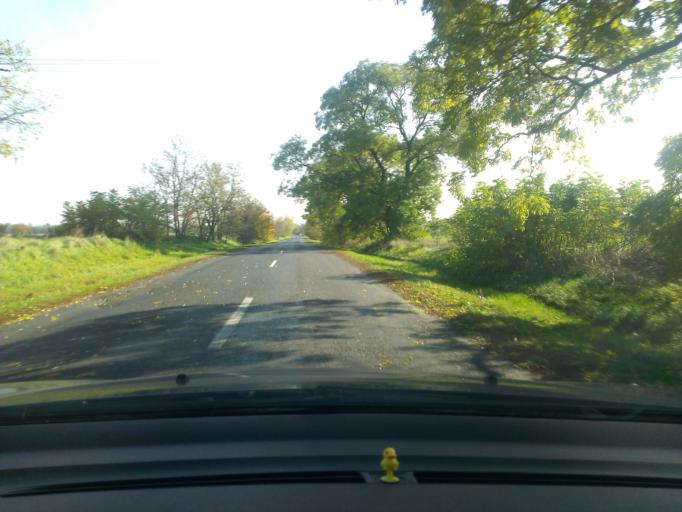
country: HU
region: Komarom-Esztergom
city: Mocsa
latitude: 47.7157
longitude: 18.1847
